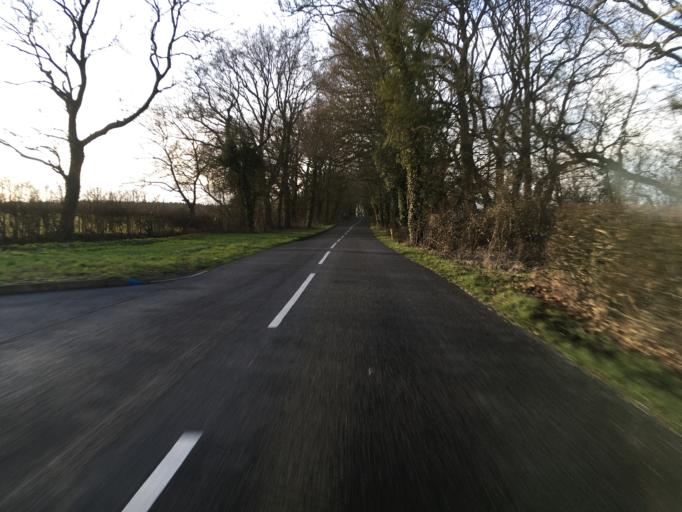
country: GB
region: England
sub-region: Warwickshire
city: Stratford-upon-Avon
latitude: 52.2285
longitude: -1.7142
